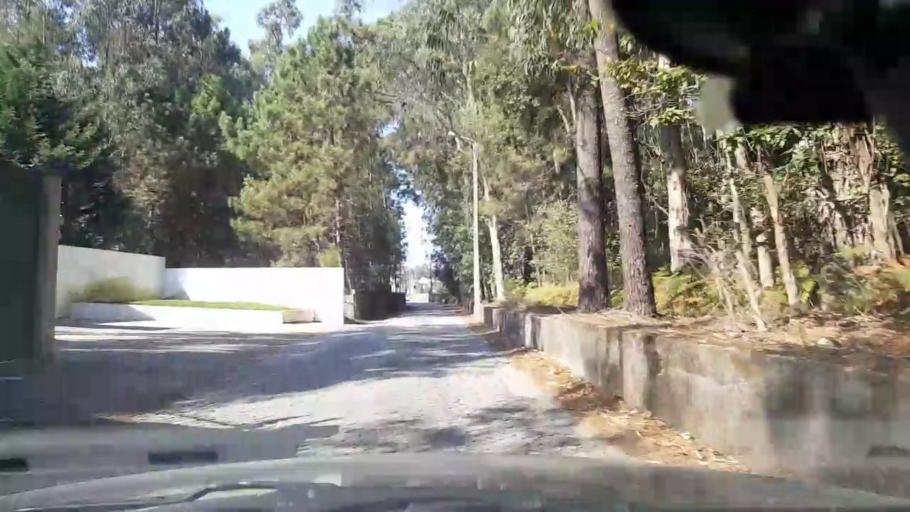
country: PT
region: Porto
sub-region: Povoa de Varzim
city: Pedroso
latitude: 41.3929
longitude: -8.7136
